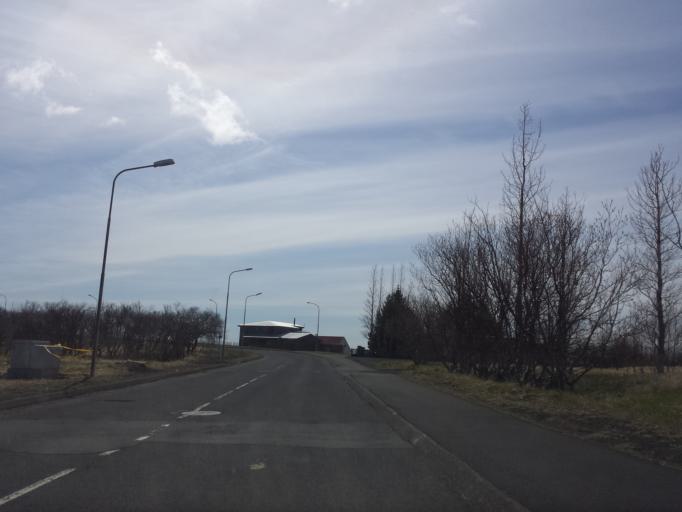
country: IS
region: South
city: Hveragerdi
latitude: 64.0069
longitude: -21.1878
